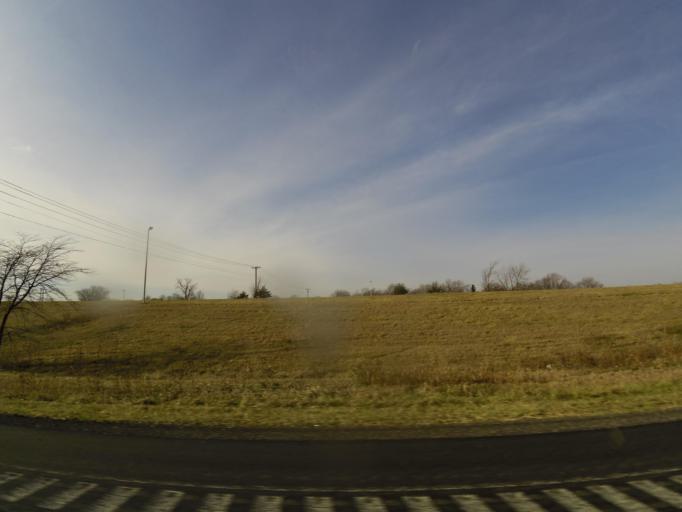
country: US
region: Illinois
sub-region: Macon County
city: Harristown
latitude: 39.8425
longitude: -89.0456
